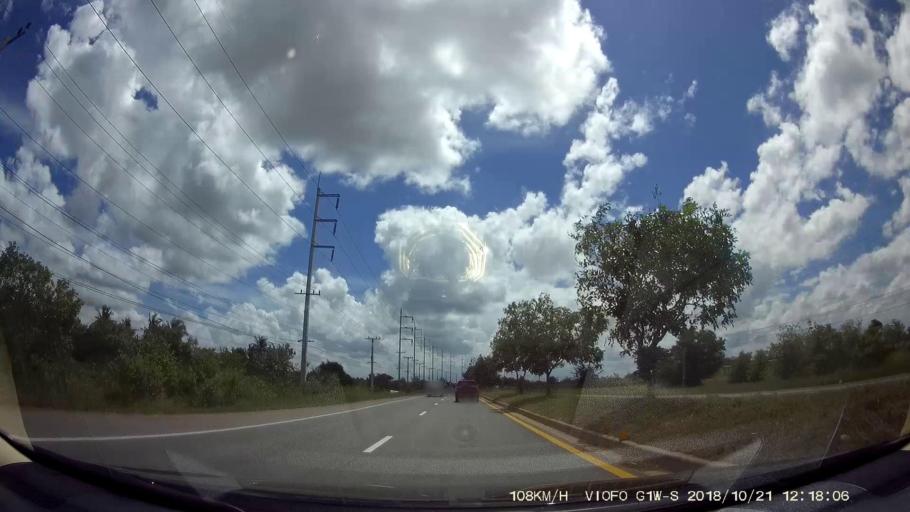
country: TH
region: Nakhon Ratchasima
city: Dan Khun Thot
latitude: 15.3221
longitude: 101.8179
